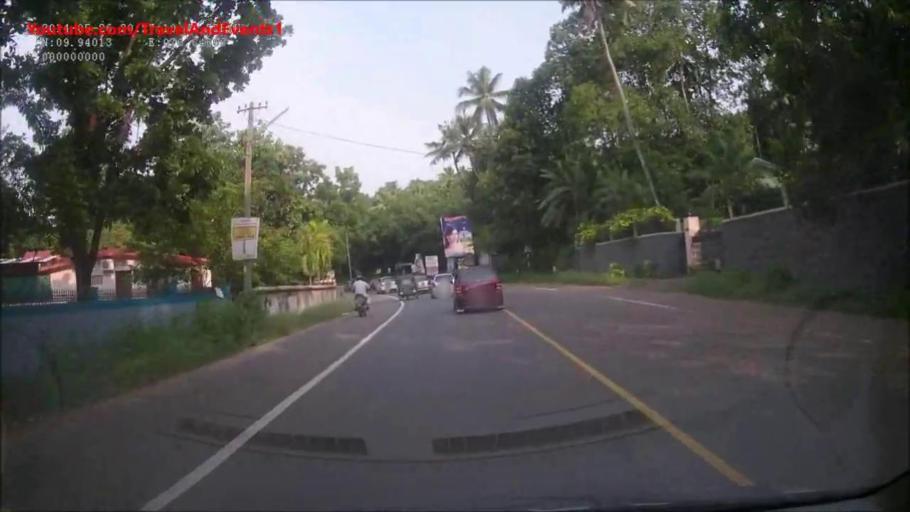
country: IN
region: Kerala
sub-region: Ernakulam
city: Muvattupula
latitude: 9.9367
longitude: 76.6545
